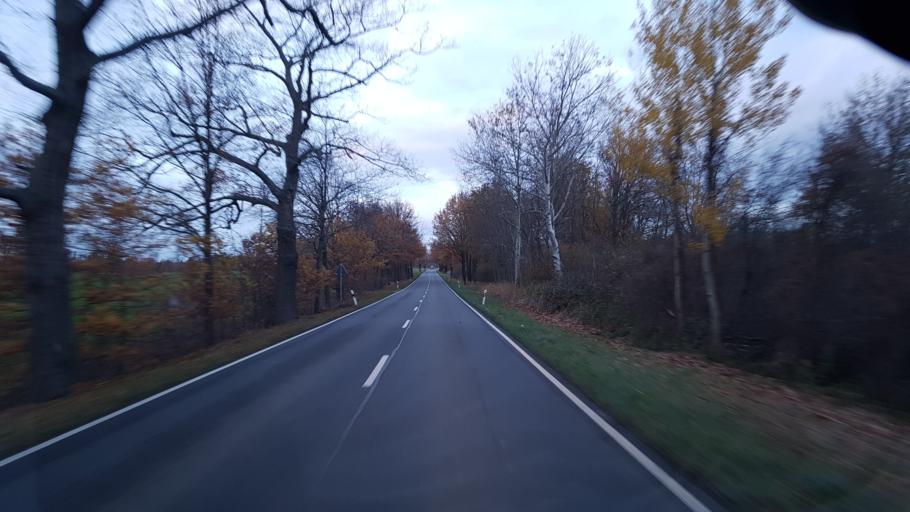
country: DE
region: Brandenburg
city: Schraden
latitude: 51.4602
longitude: 13.7119
